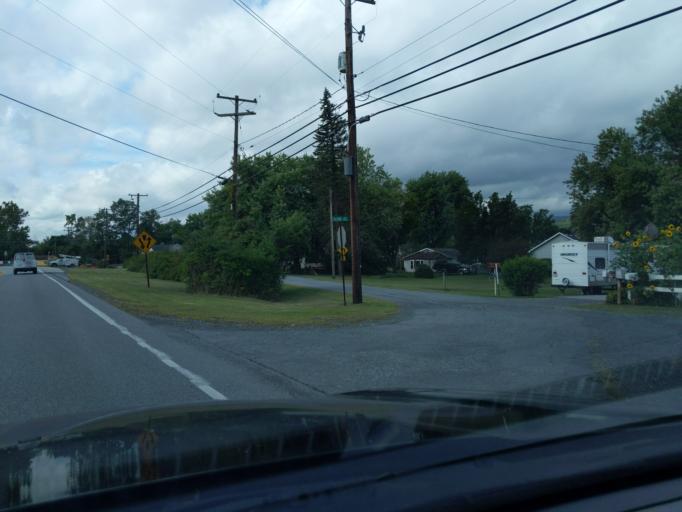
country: US
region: Pennsylvania
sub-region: Blair County
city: Roaring Spring
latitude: 40.3701
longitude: -78.4256
